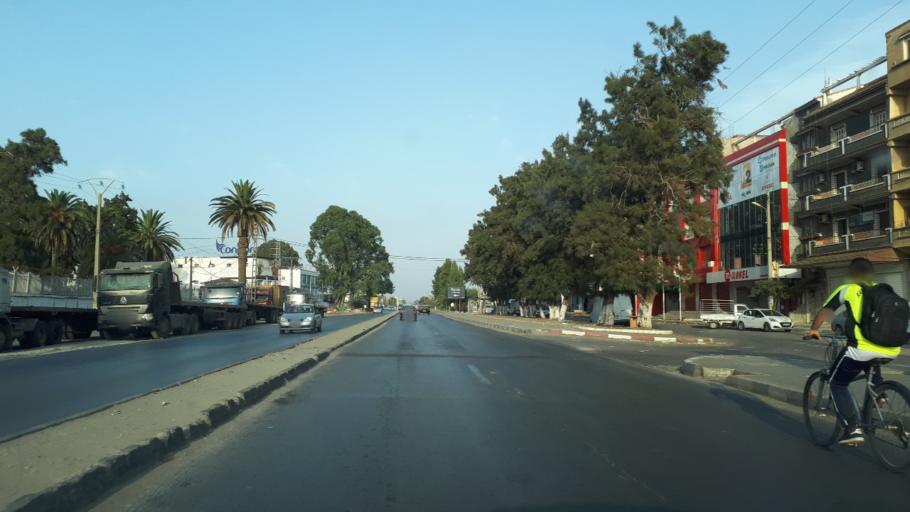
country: DZ
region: Alger
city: Dar el Beida
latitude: 36.7286
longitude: 3.2214
